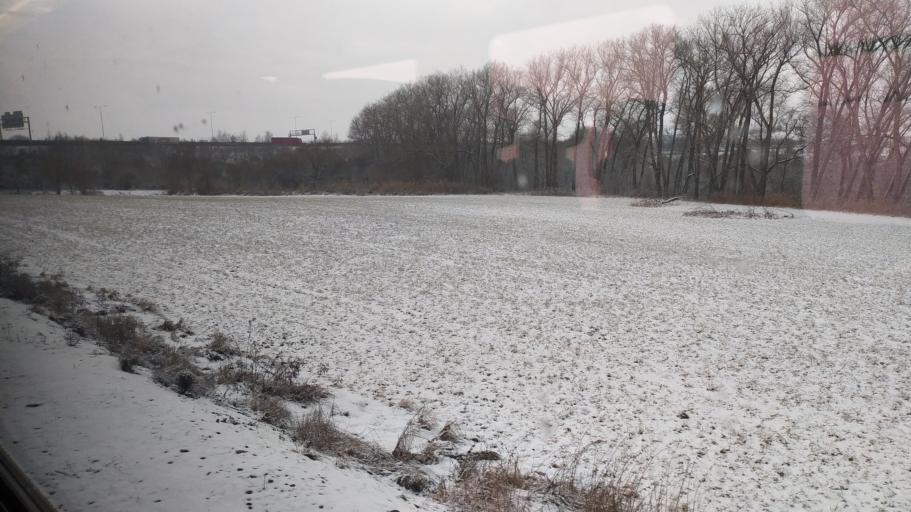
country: CZ
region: Central Bohemia
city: Trebotov
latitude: 50.0283
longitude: 14.2926
